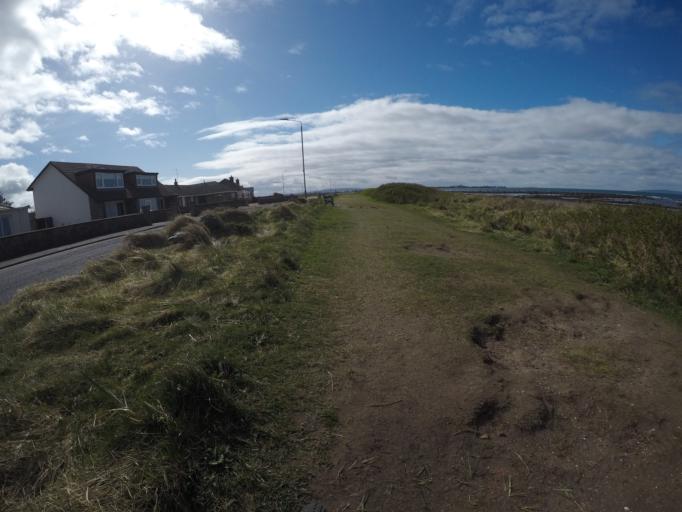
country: GB
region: Scotland
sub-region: South Ayrshire
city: Troon
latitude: 55.5670
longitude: -4.6581
